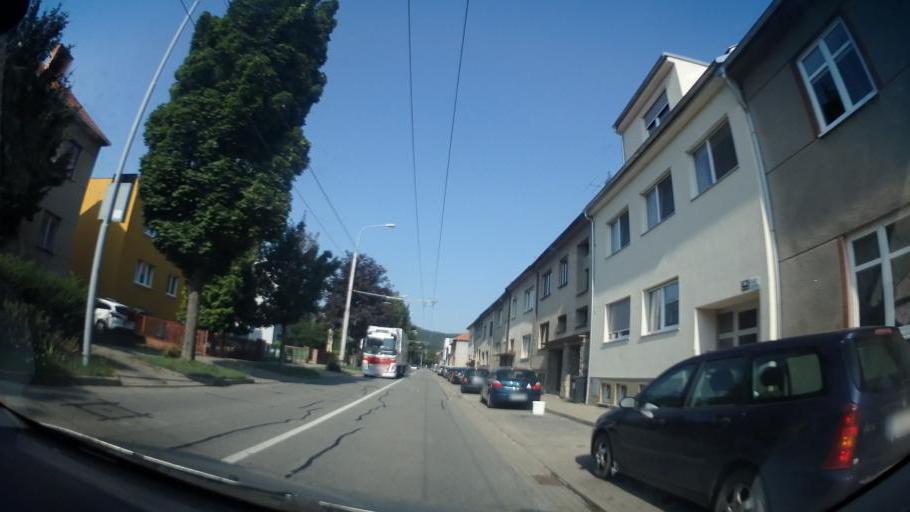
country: CZ
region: South Moravian
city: Ostopovice
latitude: 49.2053
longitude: 16.5589
